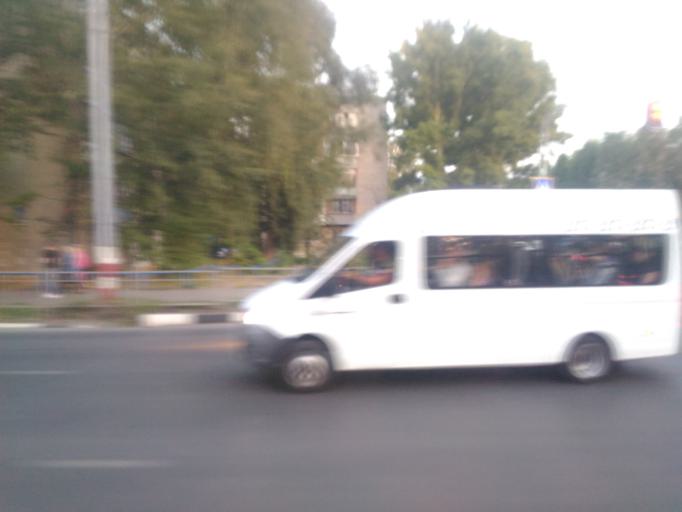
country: RU
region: Ulyanovsk
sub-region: Ulyanovskiy Rayon
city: Ulyanovsk
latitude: 54.2889
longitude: 48.3051
